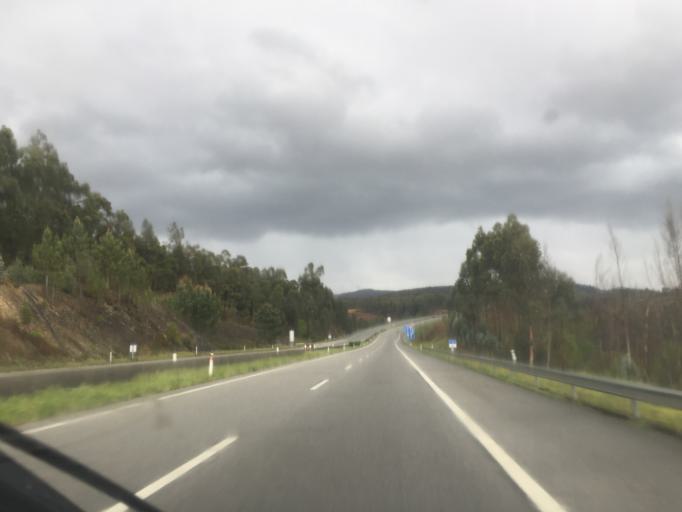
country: PT
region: Aveiro
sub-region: Agueda
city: Valongo
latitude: 40.6670
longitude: -8.4034
